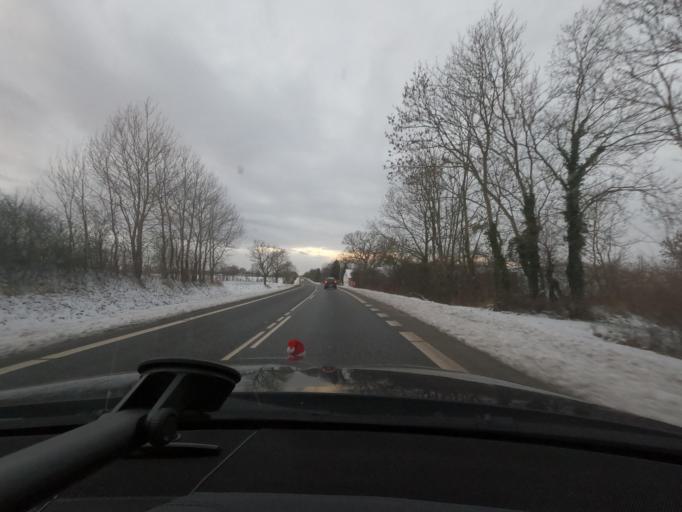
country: DE
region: Schleswig-Holstein
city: Wees
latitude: 54.8852
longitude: 9.4832
